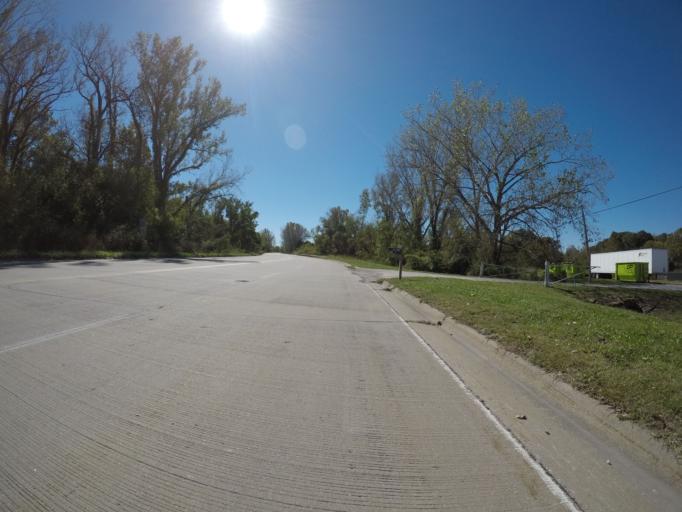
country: US
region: Kansas
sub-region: Wyandotte County
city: Bonner Springs
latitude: 39.0490
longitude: -94.8896
